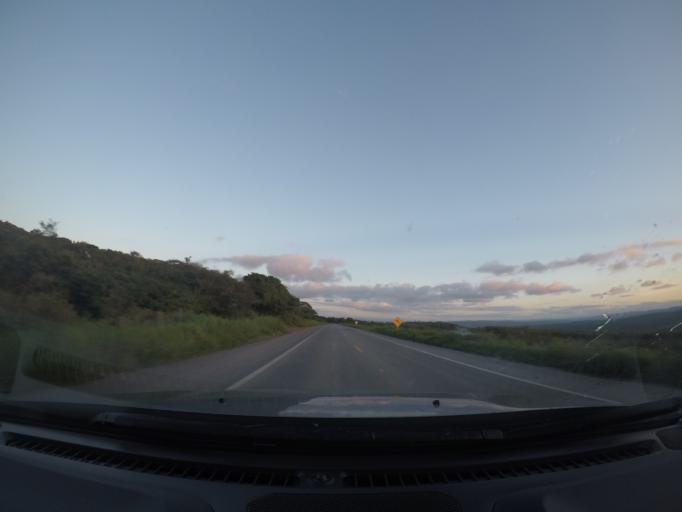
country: BR
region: Bahia
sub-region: Seabra
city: Seabra
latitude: -12.4306
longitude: -41.8265
